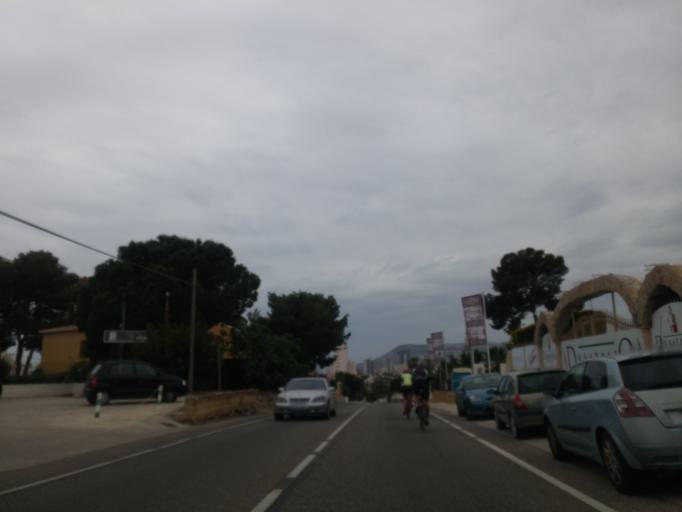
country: ES
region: Valencia
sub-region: Provincia de Alicante
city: Calp
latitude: 38.6540
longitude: 0.0761
